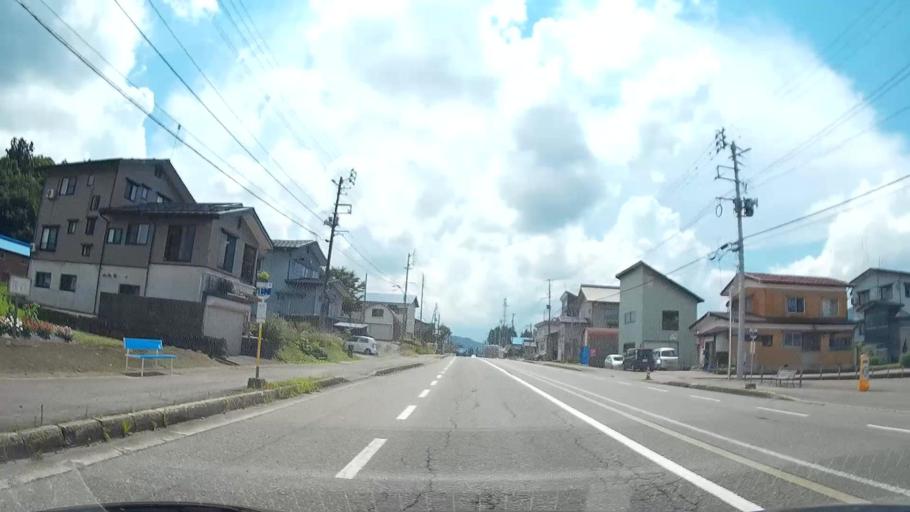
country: JP
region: Niigata
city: Tokamachi
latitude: 37.0327
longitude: 138.6696
